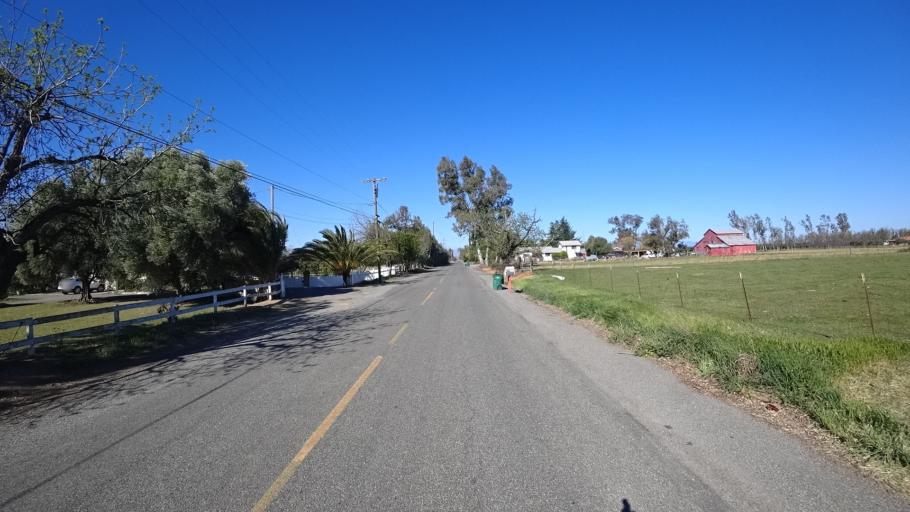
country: US
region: California
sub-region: Glenn County
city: Orland
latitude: 39.7440
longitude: -122.2202
